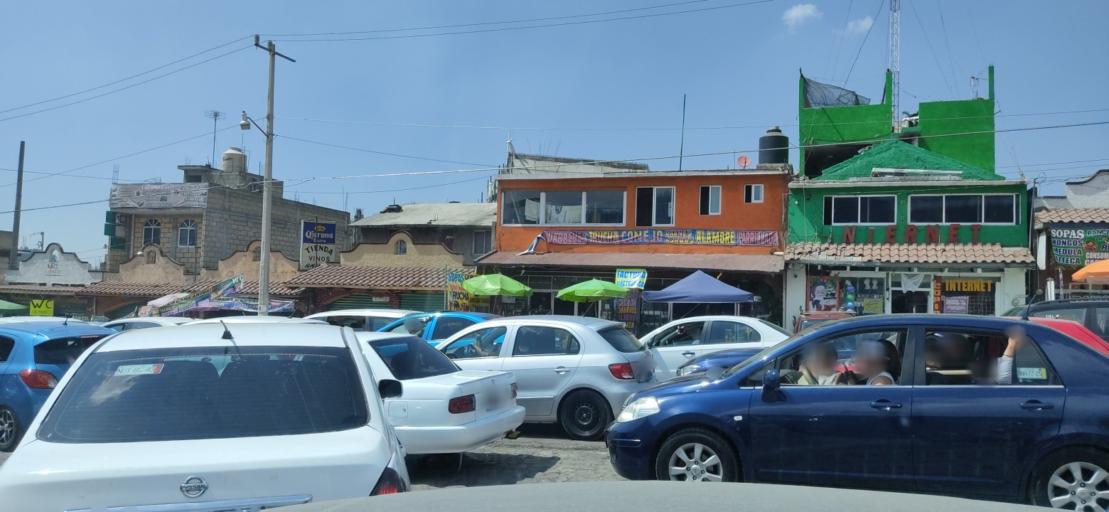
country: MX
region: Mexico
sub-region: Huixquilucan
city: El Palacio
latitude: 19.2990
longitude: -99.3716
